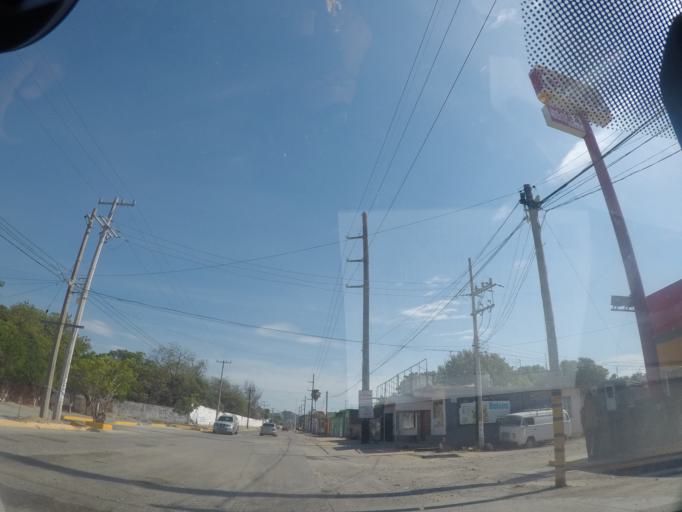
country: MX
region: Oaxaca
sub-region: Salina Cruz
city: Salina Cruz
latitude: 16.2094
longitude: -95.1955
